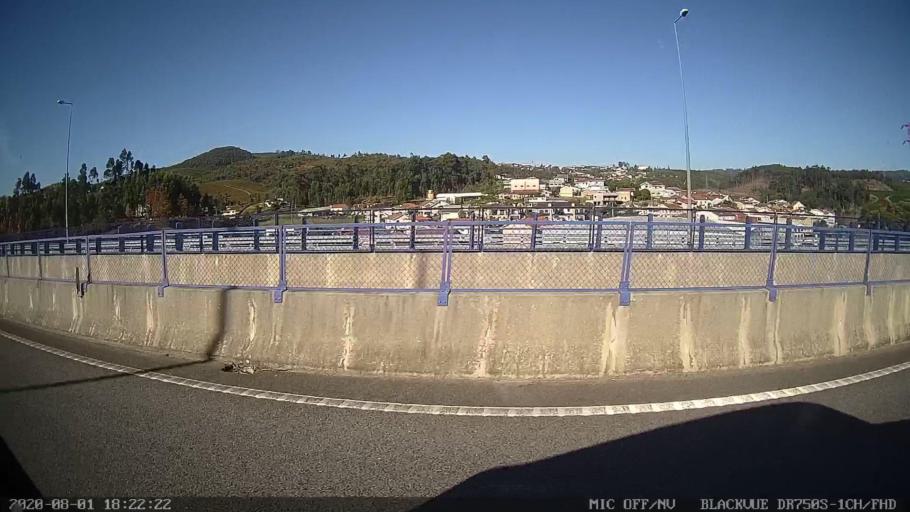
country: PT
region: Porto
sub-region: Valongo
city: Sobrado
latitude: 41.2262
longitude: -8.4527
